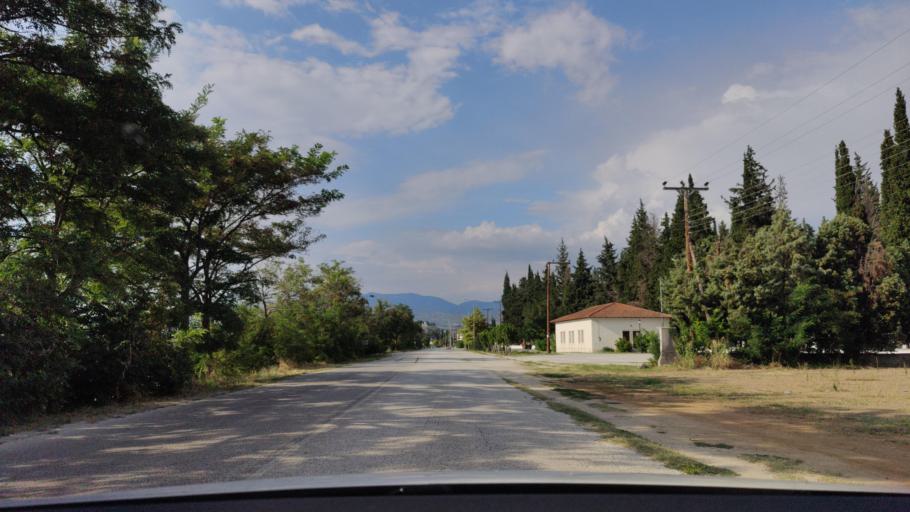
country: GR
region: Central Macedonia
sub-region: Nomos Serron
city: Sidirokastro
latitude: 41.2258
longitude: 23.3906
